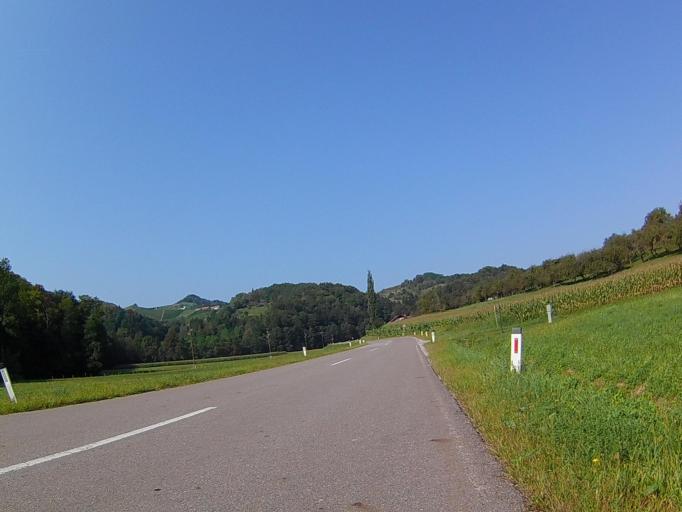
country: AT
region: Styria
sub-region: Politischer Bezirk Leibnitz
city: Sulztal an der Weinstrasse
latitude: 46.6461
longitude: 15.5597
